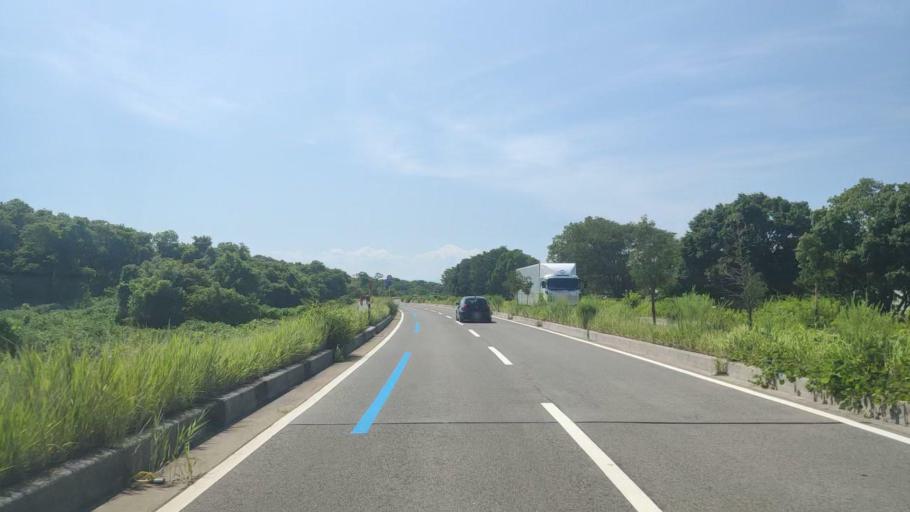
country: JP
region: Shiga Prefecture
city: Nagahama
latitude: 35.3835
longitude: 136.2521
